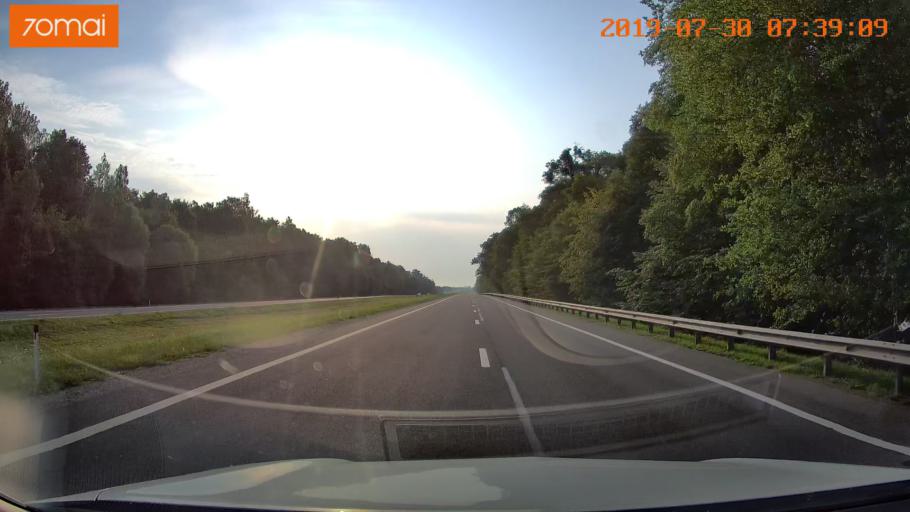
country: RU
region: Kaliningrad
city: Gvardeysk
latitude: 54.6494
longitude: 21.1878
